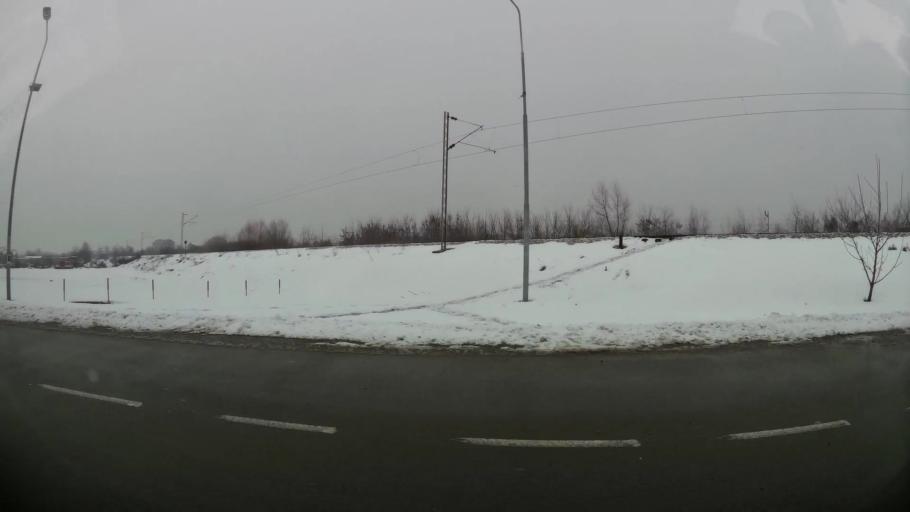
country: RS
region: Central Serbia
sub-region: Belgrade
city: Zemun
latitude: 44.8453
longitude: 20.3486
